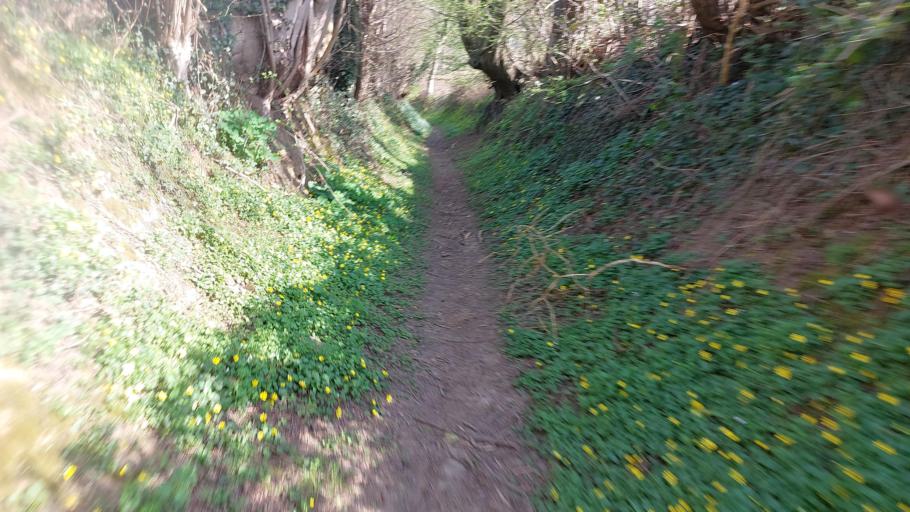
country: BE
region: Wallonia
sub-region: Province du Hainaut
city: Roeulx
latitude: 50.4980
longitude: 4.0641
